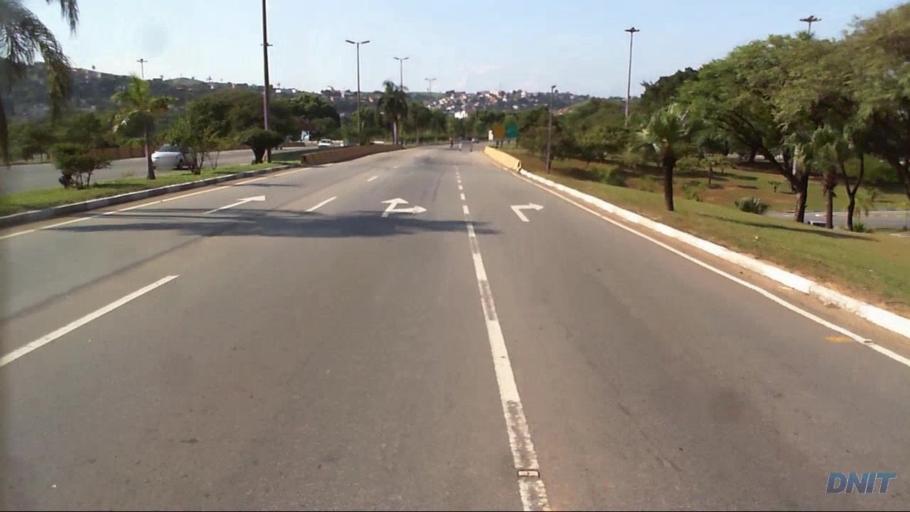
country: BR
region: Minas Gerais
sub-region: Ipatinga
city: Ipatinga
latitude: -19.4744
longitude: -42.5418
